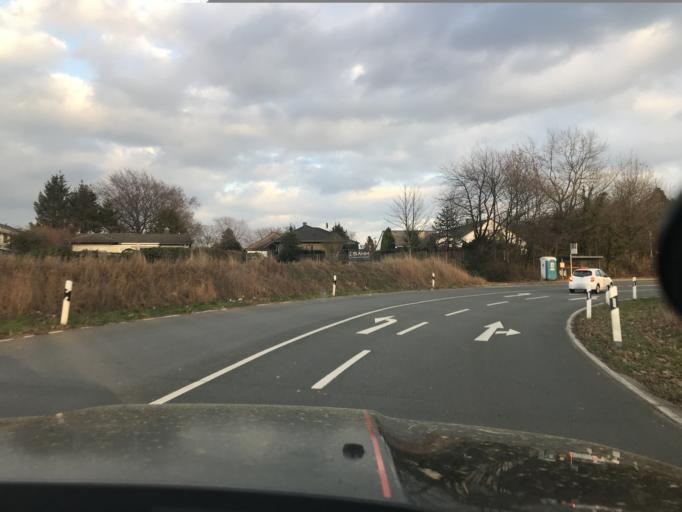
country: DE
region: North Rhine-Westphalia
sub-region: Regierungsbezirk Dusseldorf
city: Ratingen
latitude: 51.3604
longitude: 6.8657
